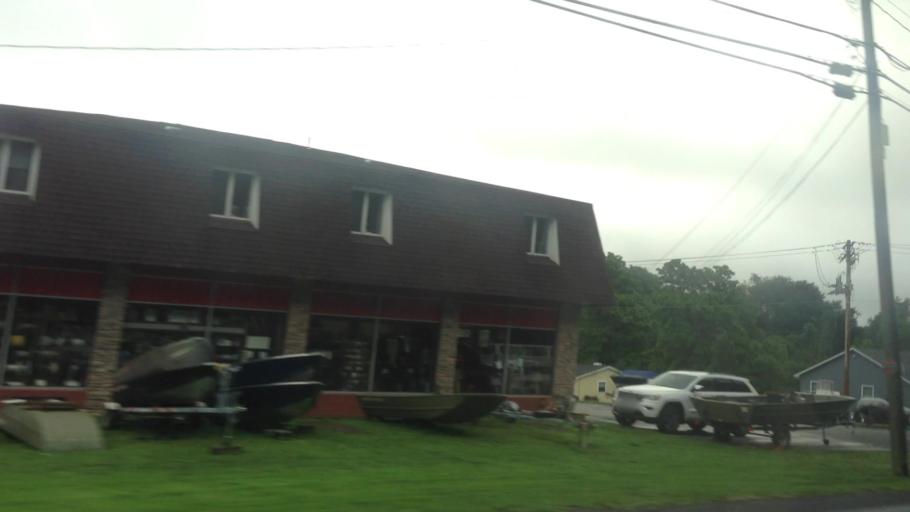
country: US
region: New York
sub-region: Ulster County
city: Lake Katrine
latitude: 41.9648
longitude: -73.9712
